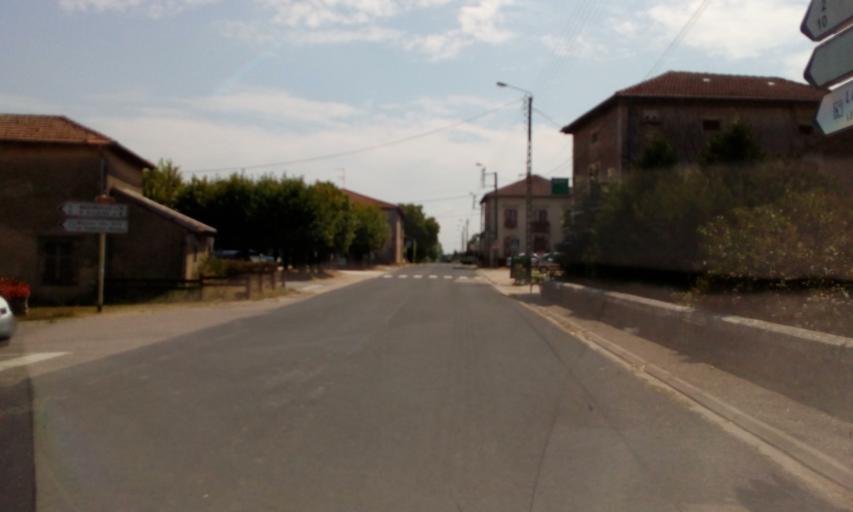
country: FR
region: Lorraine
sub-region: Departement de la Meuse
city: Vigneulles-les-Hattonchatel
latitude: 49.0389
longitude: 5.6575
